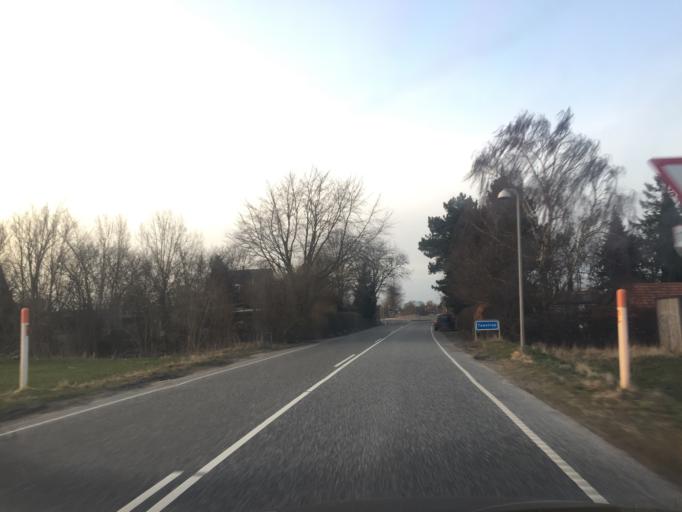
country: DK
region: Capital Region
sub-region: Hoje-Taastrup Kommune
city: Taastrup
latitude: 55.6363
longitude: 12.3083
